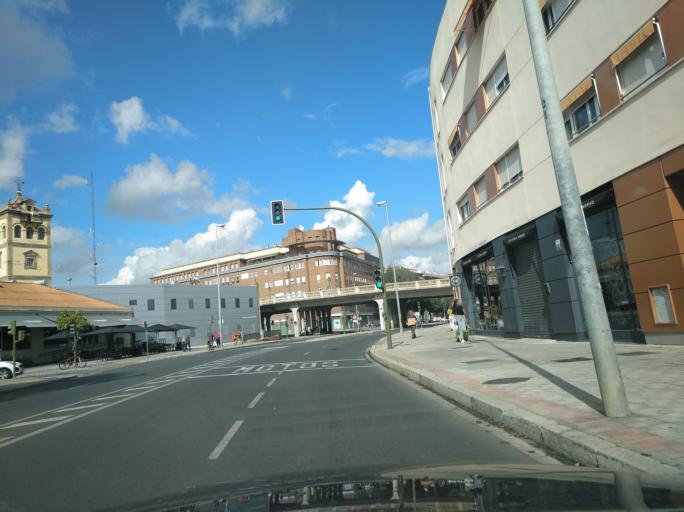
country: ES
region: Andalusia
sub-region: Provincia de Sevilla
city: Sevilla
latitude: 37.3840
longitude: -5.9840
